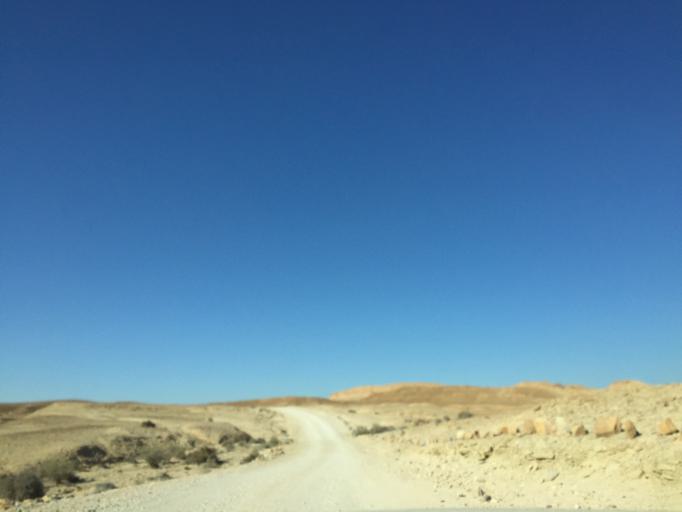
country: IL
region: Southern District
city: Mitzpe Ramon
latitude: 30.6095
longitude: 34.9364
